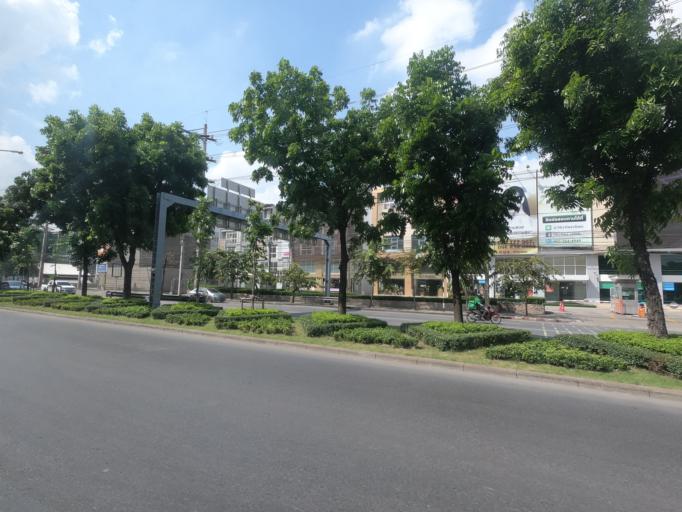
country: TH
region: Bangkok
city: Huai Khwang
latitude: 13.8006
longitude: 100.5746
